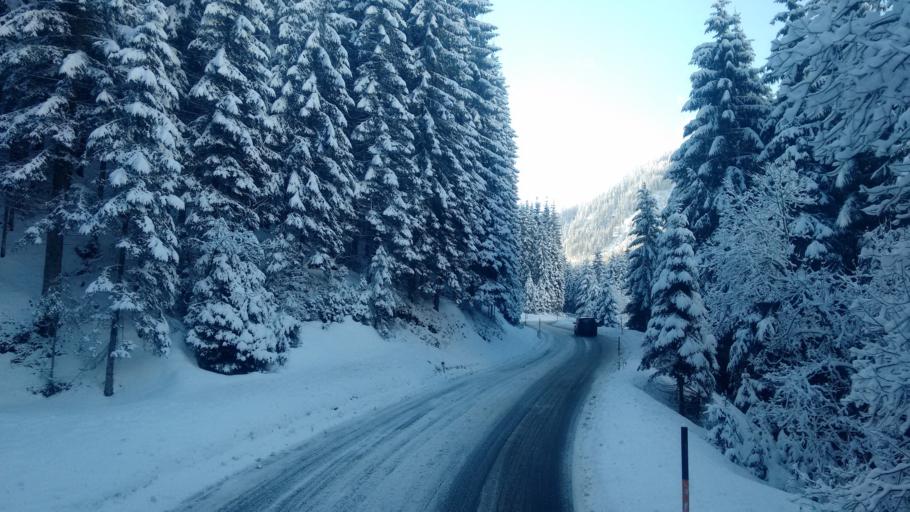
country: AT
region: Salzburg
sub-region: Politischer Bezirk Sankt Johann im Pongau
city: Untertauern
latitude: 47.3177
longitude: 13.4484
